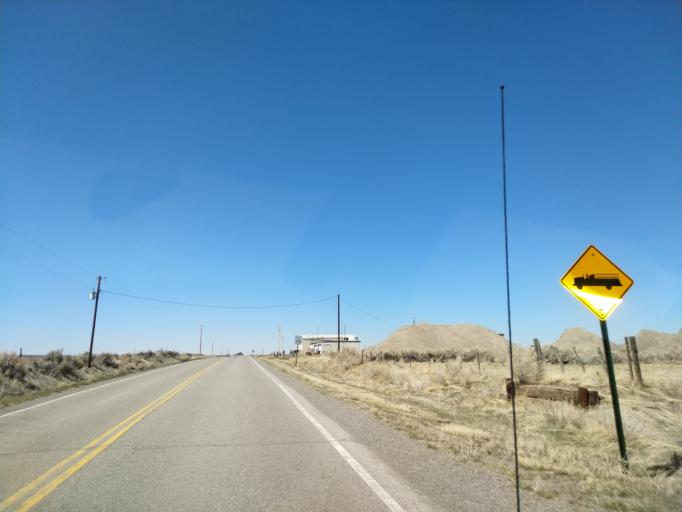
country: US
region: Colorado
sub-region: Mesa County
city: Redlands
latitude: 38.9938
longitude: -108.7415
